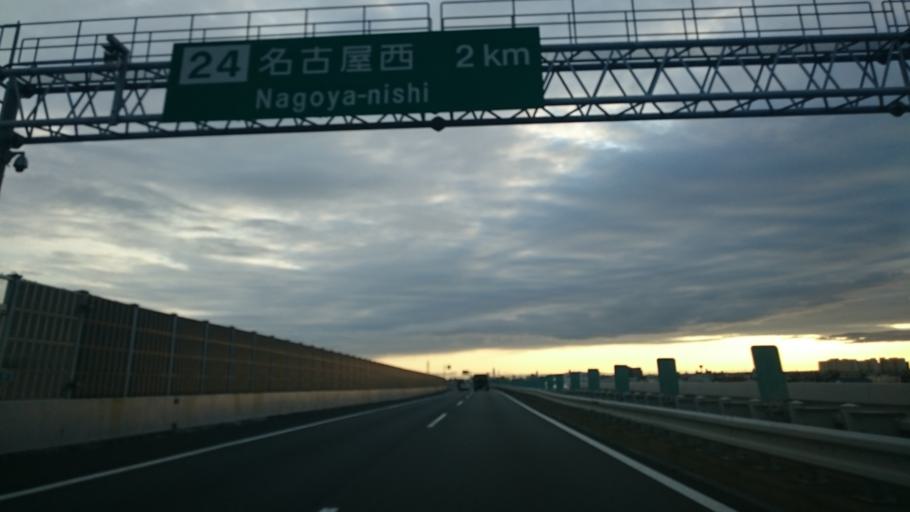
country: JP
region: Aichi
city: Kanie
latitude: 35.1494
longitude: 136.7890
